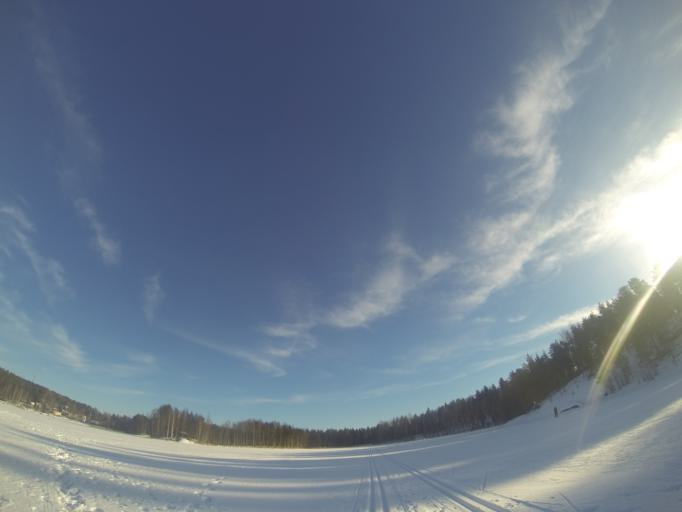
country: FI
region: Southern Savonia
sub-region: Savonlinna
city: Savonlinna
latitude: 61.8804
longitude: 28.9165
